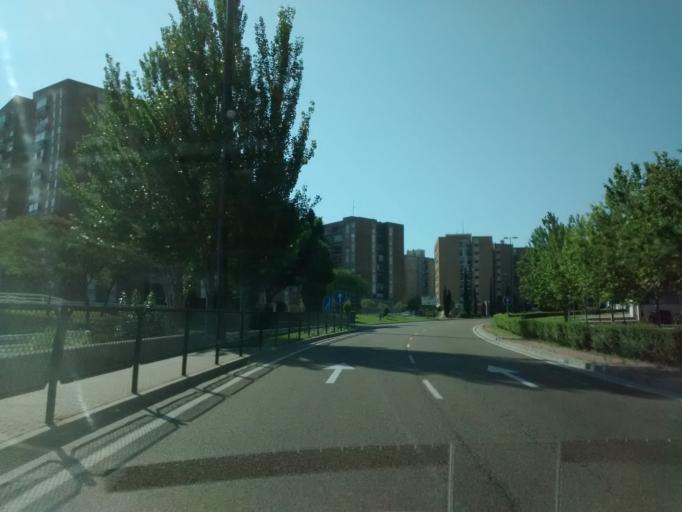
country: ES
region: Aragon
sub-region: Provincia de Zaragoza
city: Delicias
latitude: 41.6582
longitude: -0.9224
